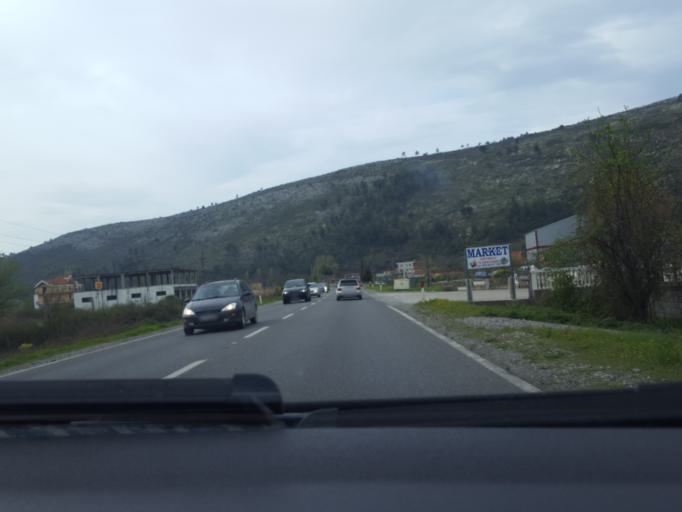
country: AL
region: Lezhe
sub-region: Rrethi i Lezhes
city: Balldreni i Ri
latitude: 41.8064
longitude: 19.6327
